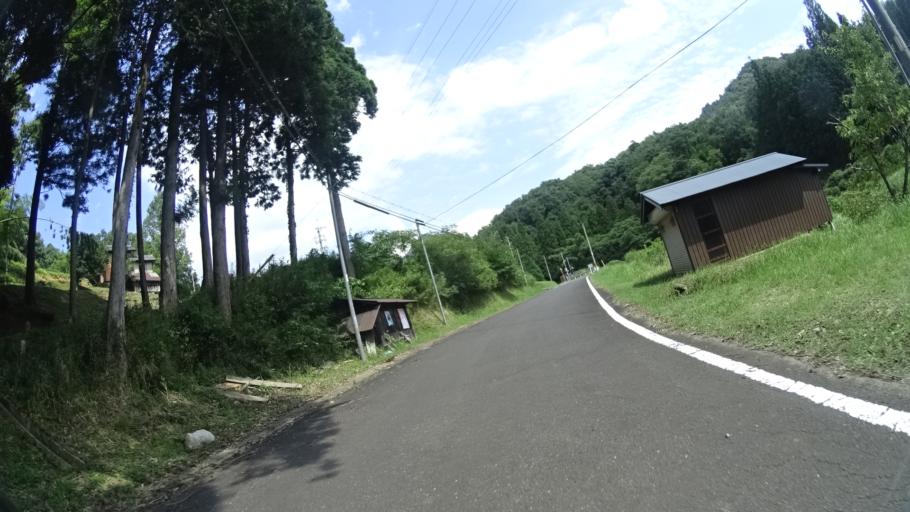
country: JP
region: Kyoto
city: Maizuru
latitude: 35.3832
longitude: 135.3551
